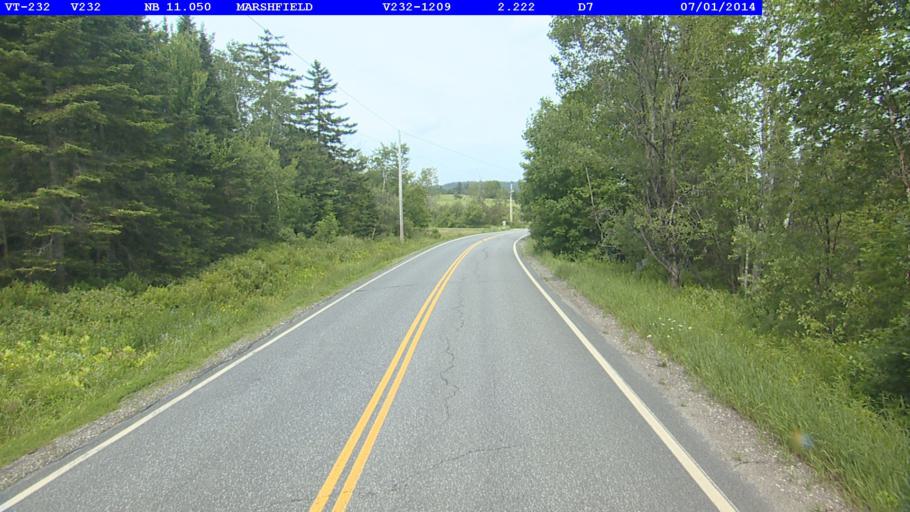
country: US
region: Vermont
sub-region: Caledonia County
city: Hardwick
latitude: 44.3402
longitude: -72.2924
